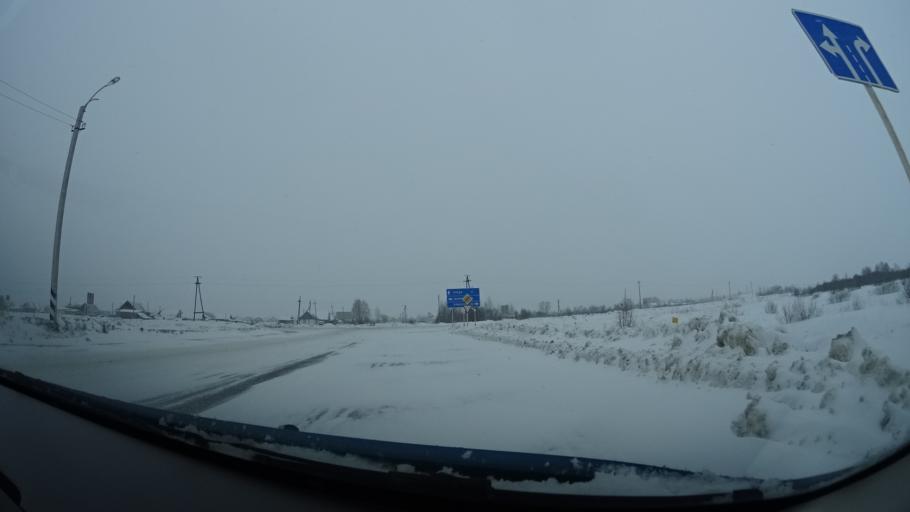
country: RU
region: Perm
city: Kuyeda
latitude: 56.4498
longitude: 55.6014
